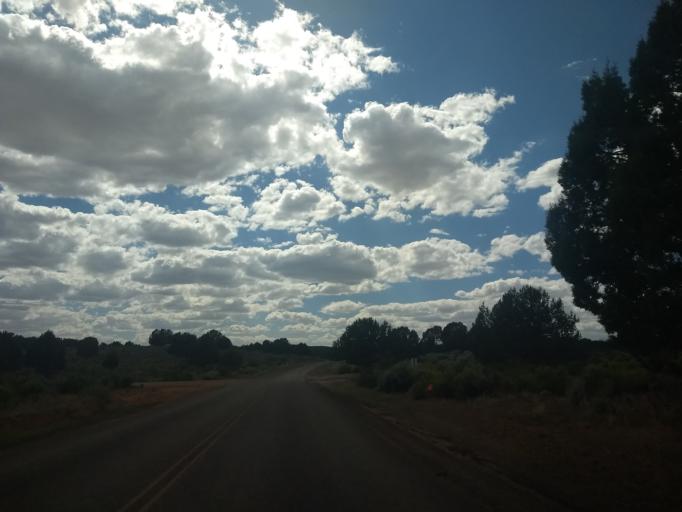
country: US
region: Utah
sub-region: Kane County
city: Kanab
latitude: 37.1454
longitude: -112.5605
